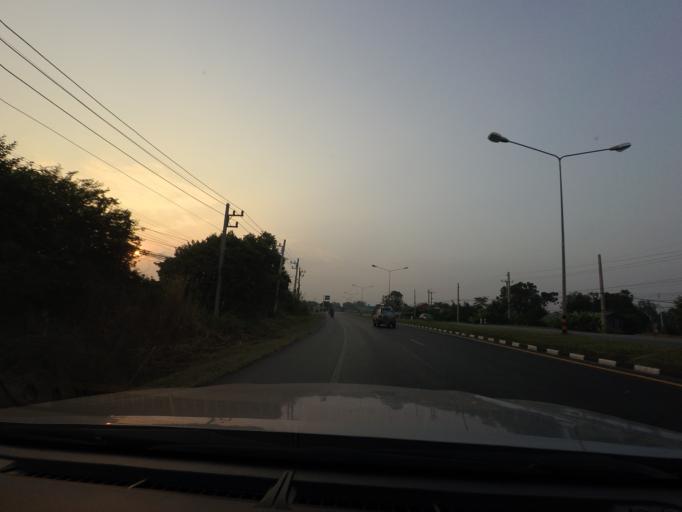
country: TH
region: Phitsanulok
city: Wang Thong
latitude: 16.8181
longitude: 100.4373
